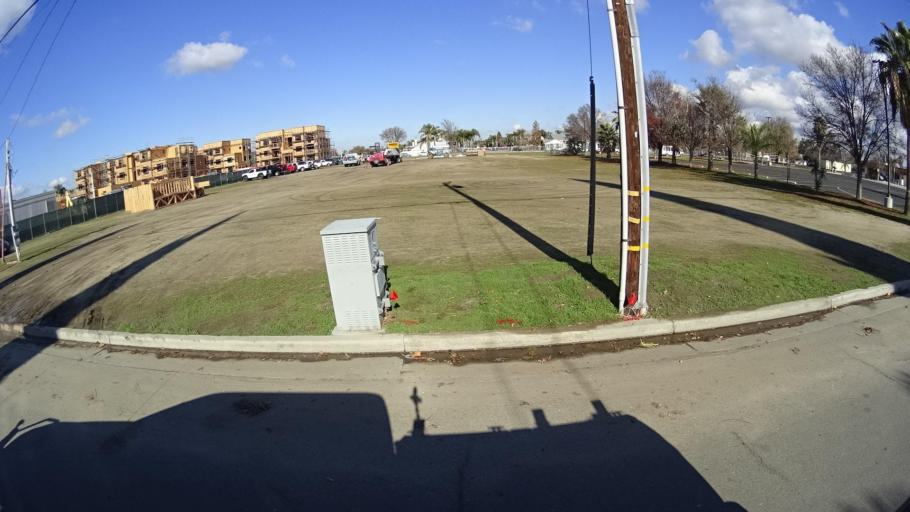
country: US
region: California
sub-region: Kern County
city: McFarland
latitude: 35.6742
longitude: -119.2369
